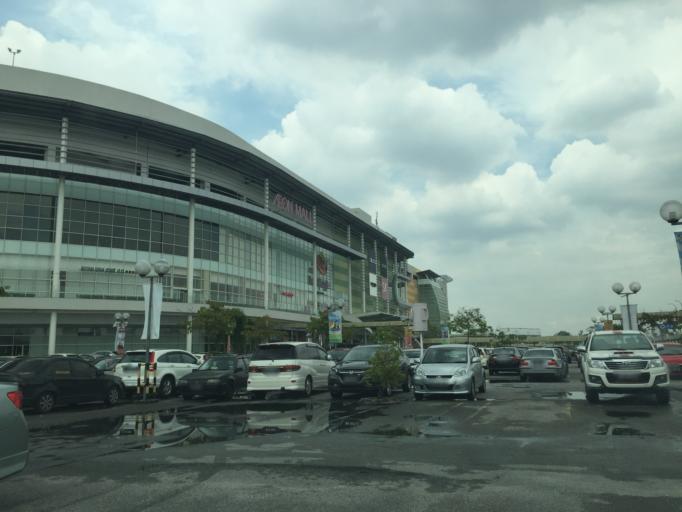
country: MY
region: Selangor
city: Klang
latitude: 2.9932
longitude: 101.4459
